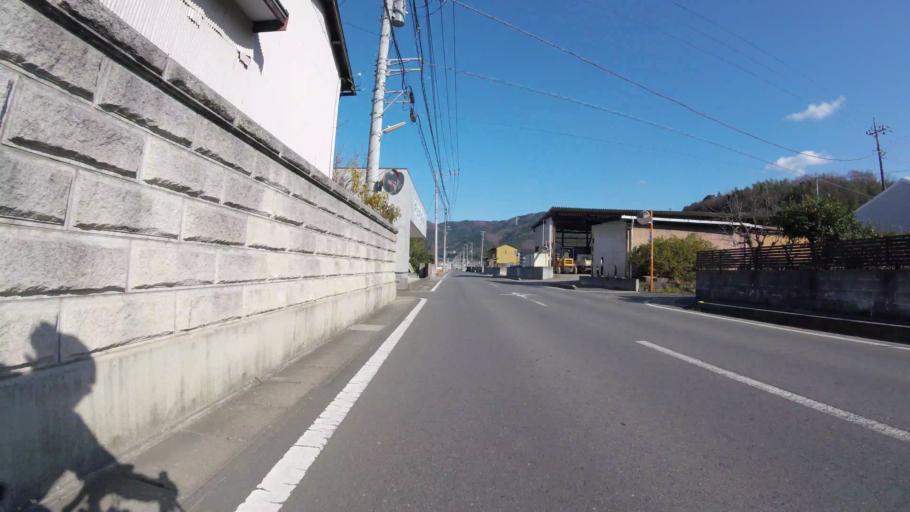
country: JP
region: Shizuoka
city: Mishima
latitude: 35.0678
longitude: 138.9574
